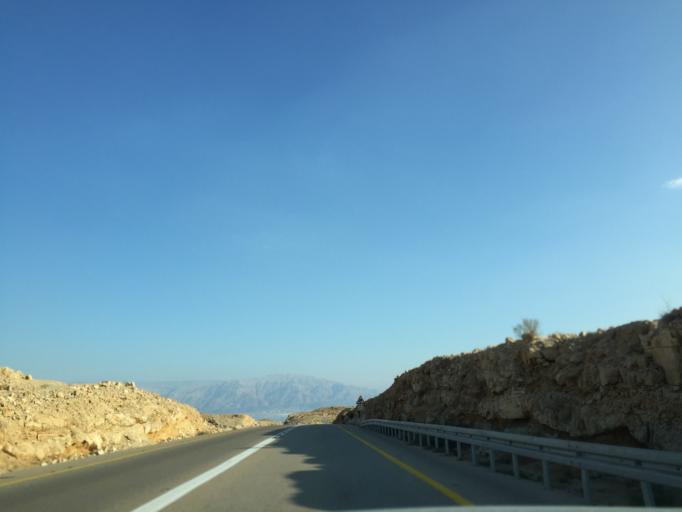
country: IL
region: Southern District
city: `En Boqeq
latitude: 31.1624
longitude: 35.3247
